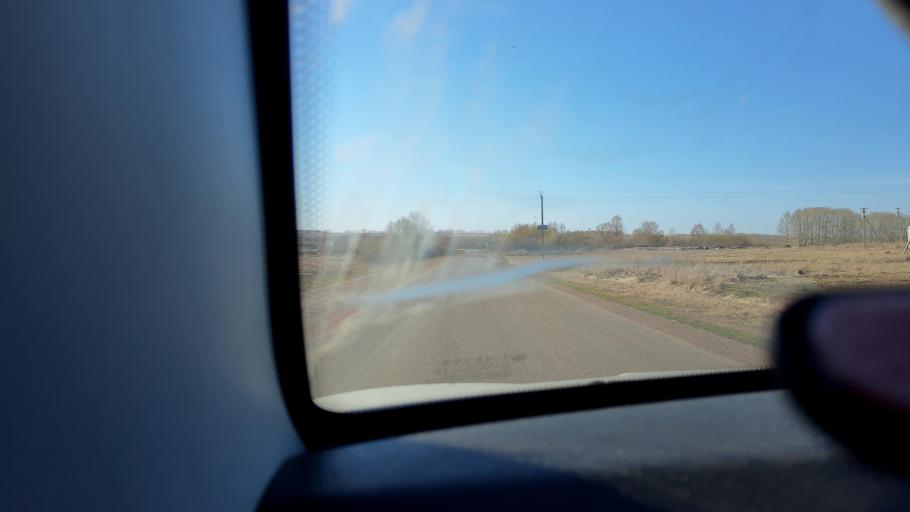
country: RU
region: Bashkortostan
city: Asanovo
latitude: 54.8467
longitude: 55.4586
